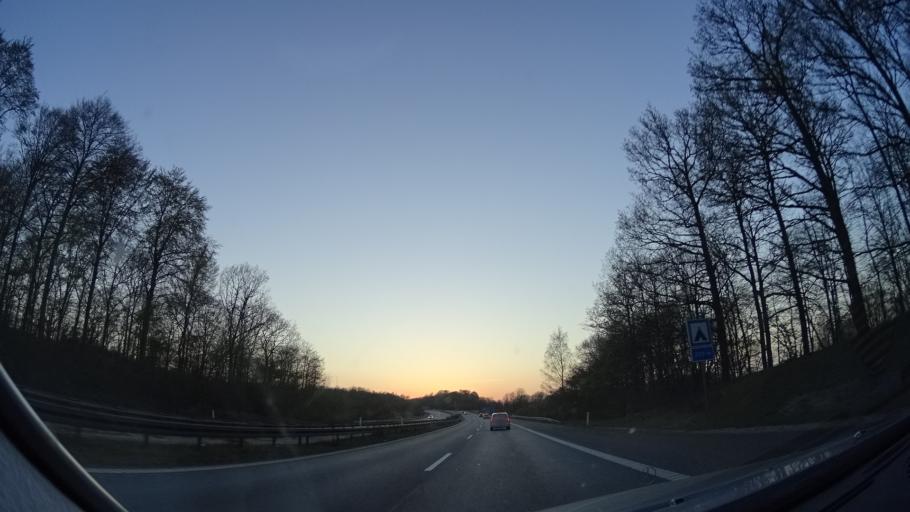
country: DK
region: Zealand
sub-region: Lejre Kommune
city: Lejre
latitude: 55.6475
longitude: 11.9307
